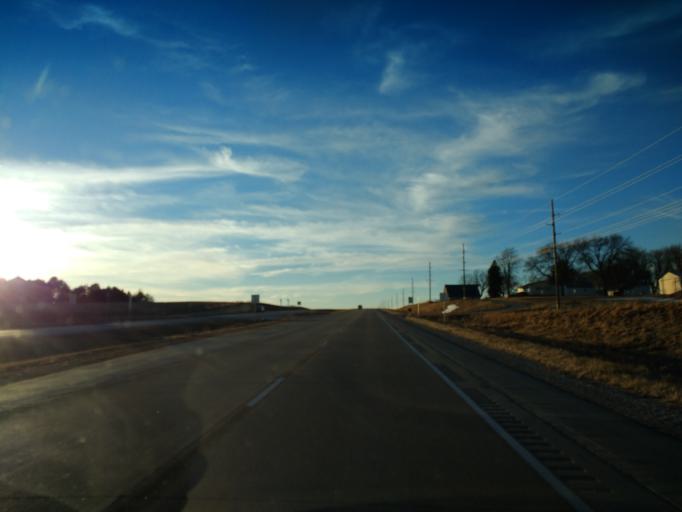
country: US
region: Iowa
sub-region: Ida County
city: Holstein
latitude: 42.4751
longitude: -95.4765
